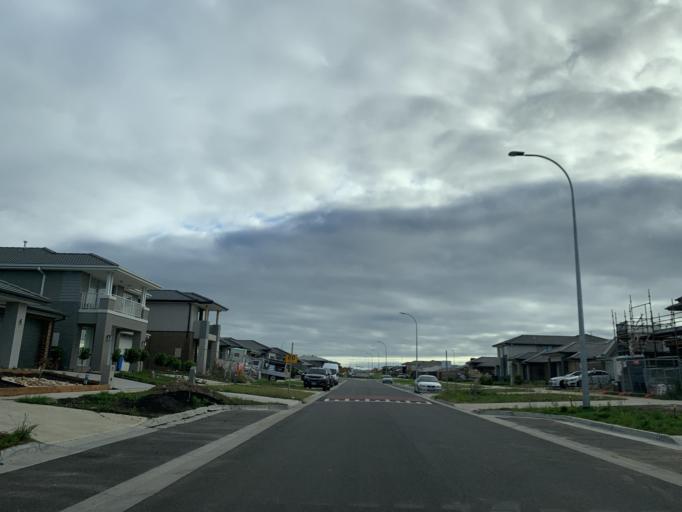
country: AU
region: Victoria
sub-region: Casey
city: Cranbourne East
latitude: -38.1263
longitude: 145.3356
